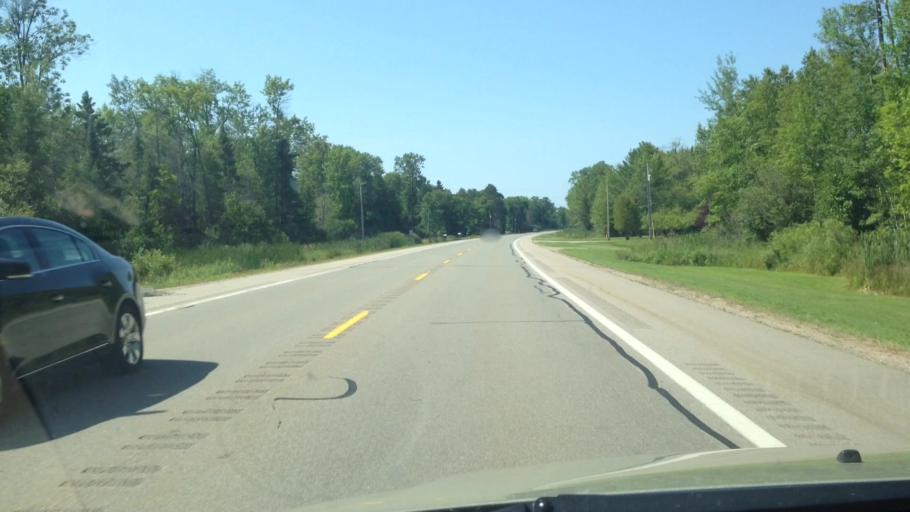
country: US
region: Michigan
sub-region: Menominee County
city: Menominee
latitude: 45.2218
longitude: -87.5155
